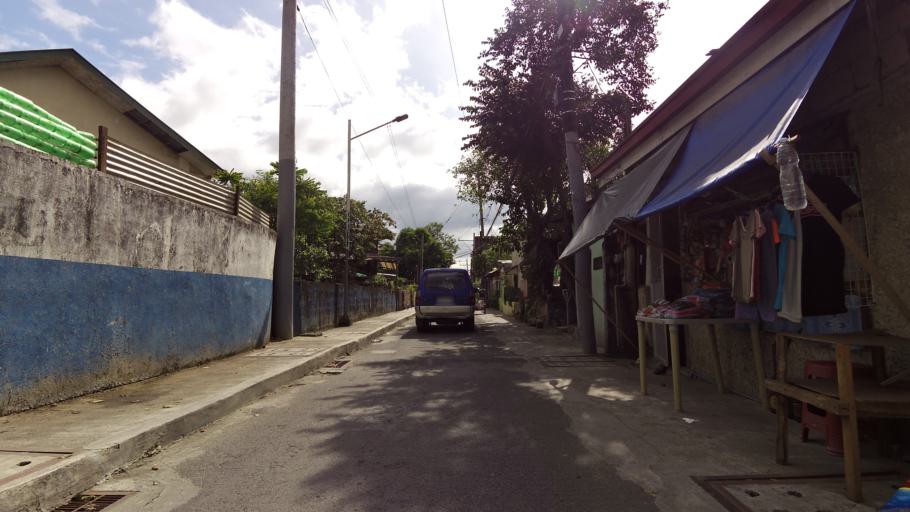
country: PH
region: Calabarzon
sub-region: Province of Rizal
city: Cainta
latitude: 14.5752
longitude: 121.1172
